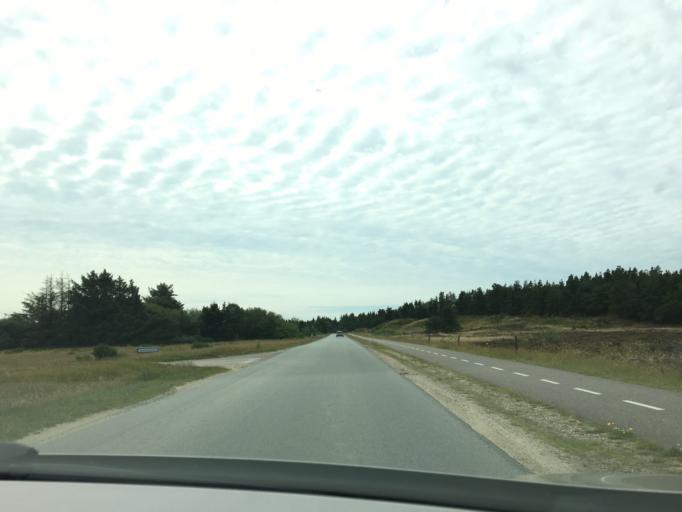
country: DK
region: South Denmark
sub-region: Varde Kommune
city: Oksbol
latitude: 55.7307
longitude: 8.2135
